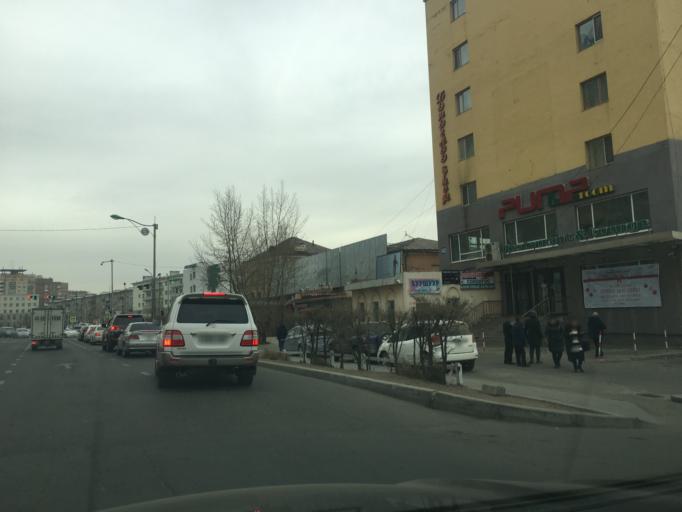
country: MN
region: Ulaanbaatar
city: Ulaanbaatar
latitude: 47.9134
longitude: 106.8935
